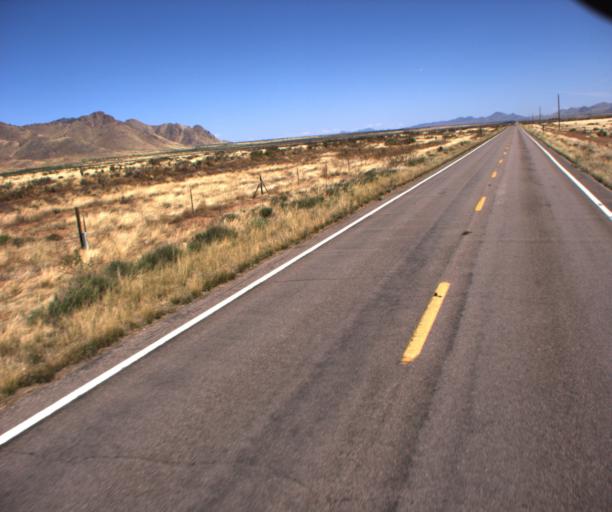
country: US
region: Arizona
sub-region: Cochise County
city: Douglas
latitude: 31.7054
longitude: -109.1225
